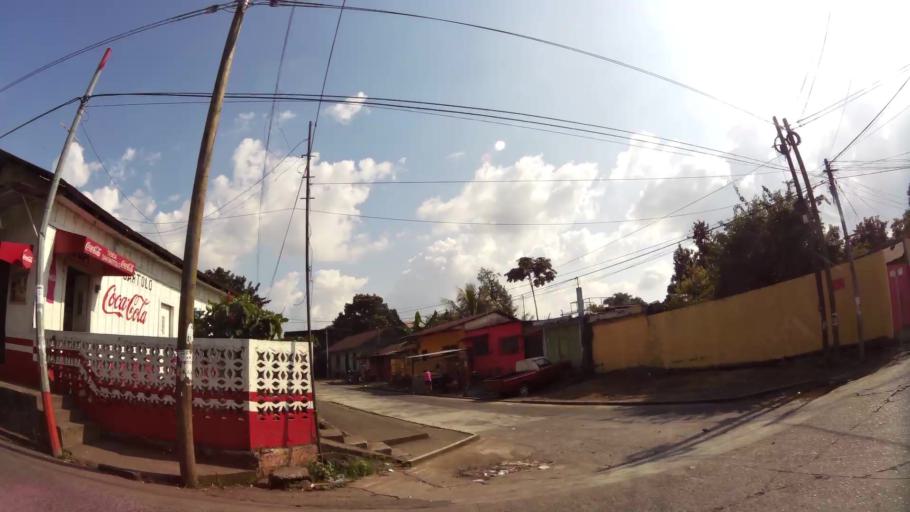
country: GT
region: Retalhuleu
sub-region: Municipio de Retalhuleu
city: Retalhuleu
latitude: 14.5398
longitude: -91.6822
